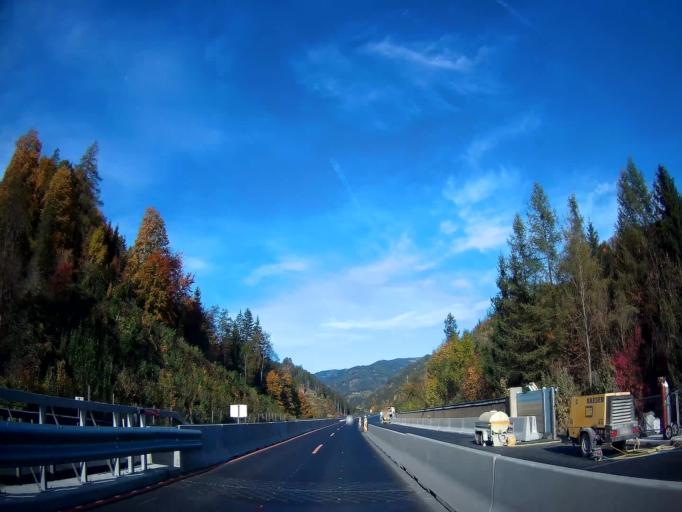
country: AT
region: Styria
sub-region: Politischer Bezirk Graz-Umgebung
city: Ubelbach
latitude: 47.2288
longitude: 15.2190
